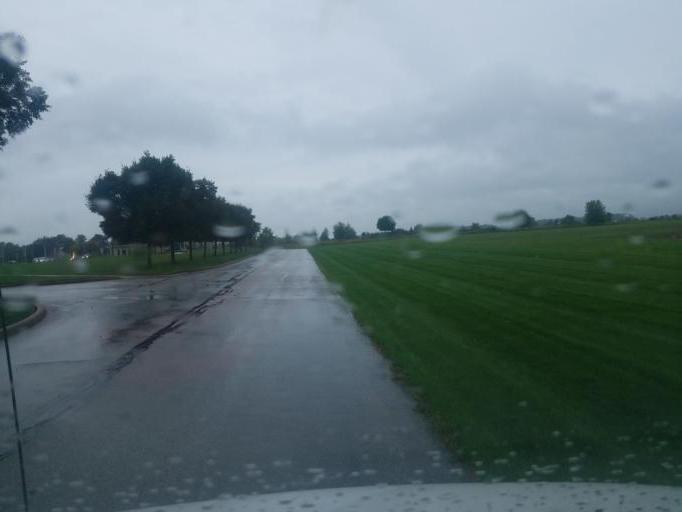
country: US
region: Ohio
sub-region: Wayne County
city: Rittman
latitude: 41.0028
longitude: -81.8102
